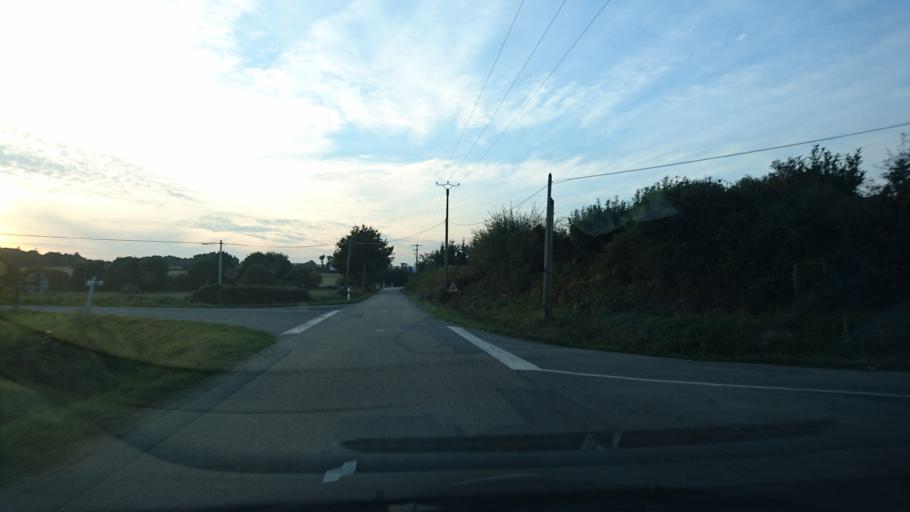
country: FR
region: Brittany
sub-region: Departement du Morbihan
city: Guer
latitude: 47.8687
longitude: -2.0722
